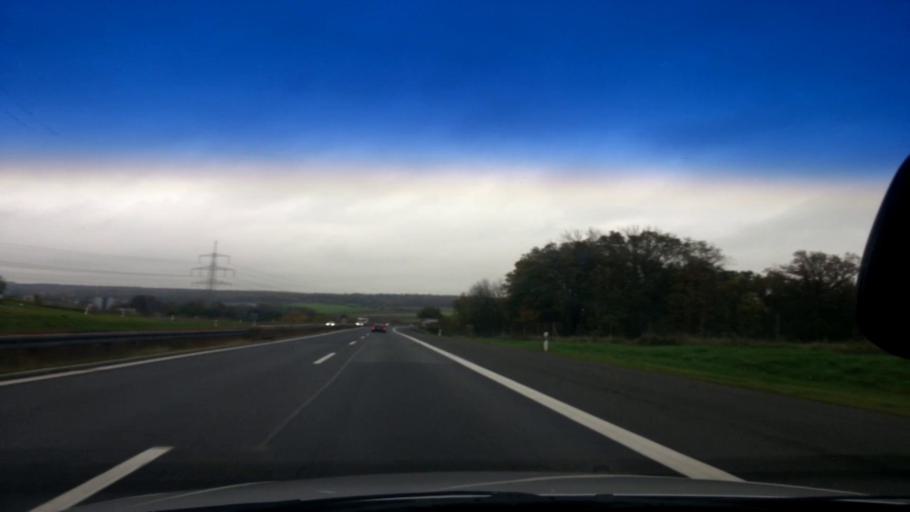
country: DE
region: Bavaria
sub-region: Upper Franconia
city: Memmelsdorf
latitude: 49.9584
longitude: 10.9849
